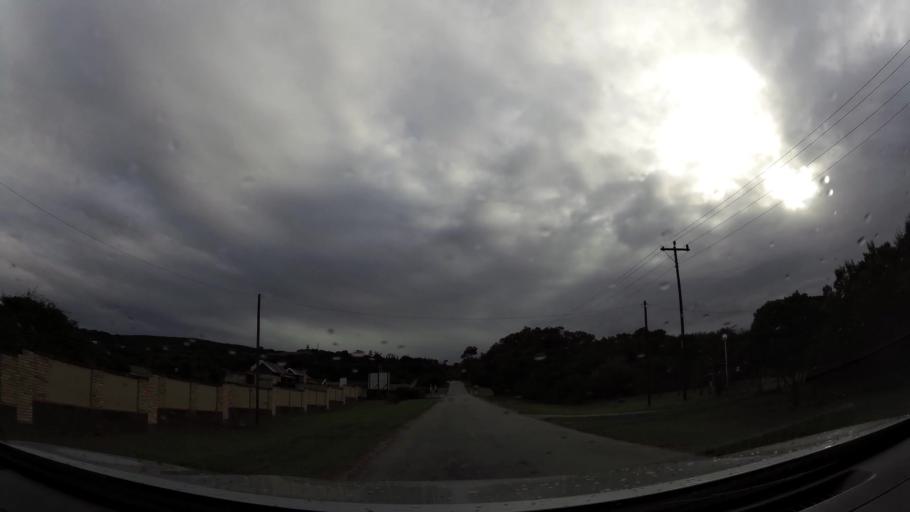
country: ZA
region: Eastern Cape
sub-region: Nelson Mandela Bay Metropolitan Municipality
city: Port Elizabeth
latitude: -34.0158
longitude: 25.4973
